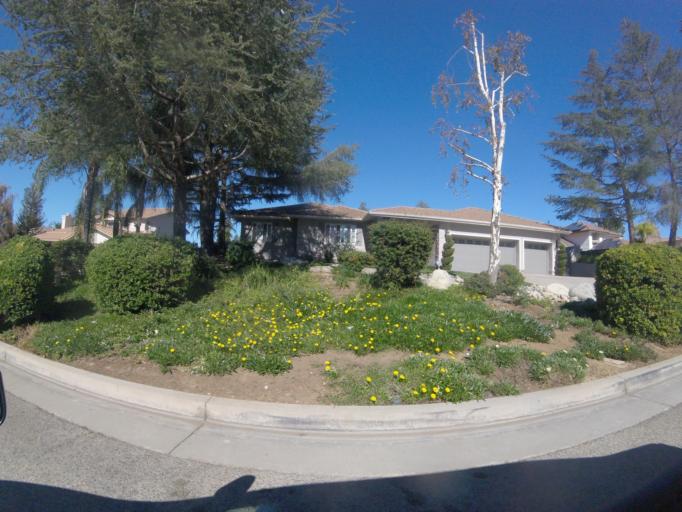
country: US
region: California
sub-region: San Bernardino County
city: Redlands
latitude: 34.0173
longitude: -117.1593
